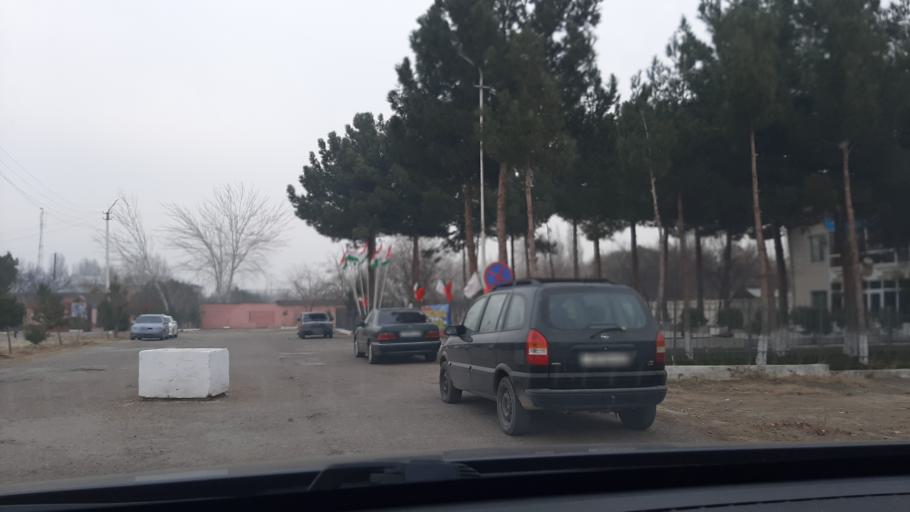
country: TJ
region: Viloyati Sughd
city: Palos
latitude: 40.2608
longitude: 69.7936
